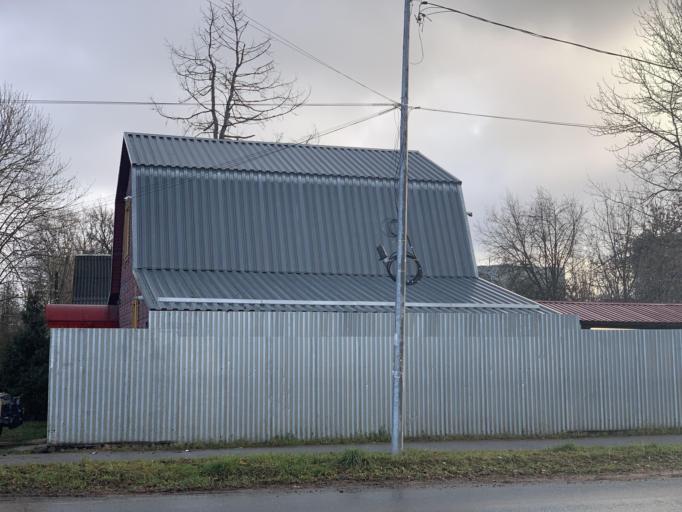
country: RU
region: Tverskaya
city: Likhoslavl'
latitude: 57.1257
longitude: 35.4623
